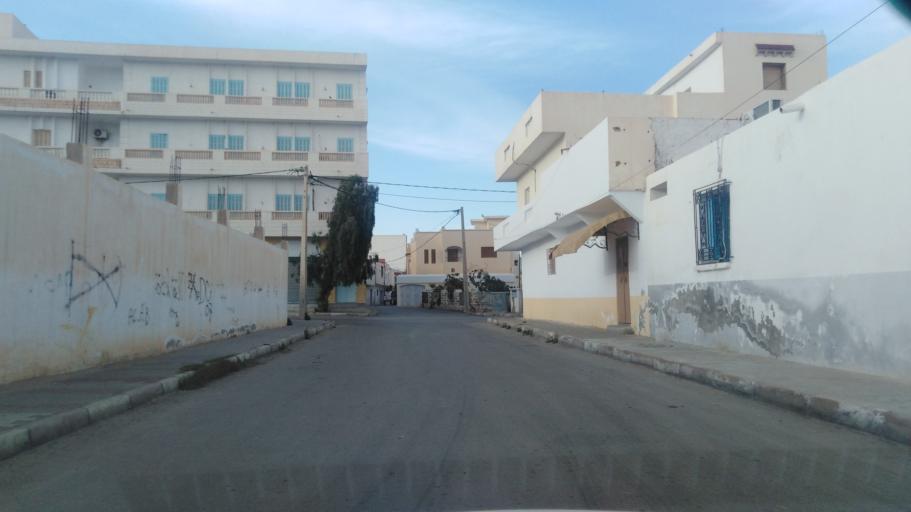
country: TN
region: Tataouine
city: Tataouine
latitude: 32.9335
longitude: 10.4520
